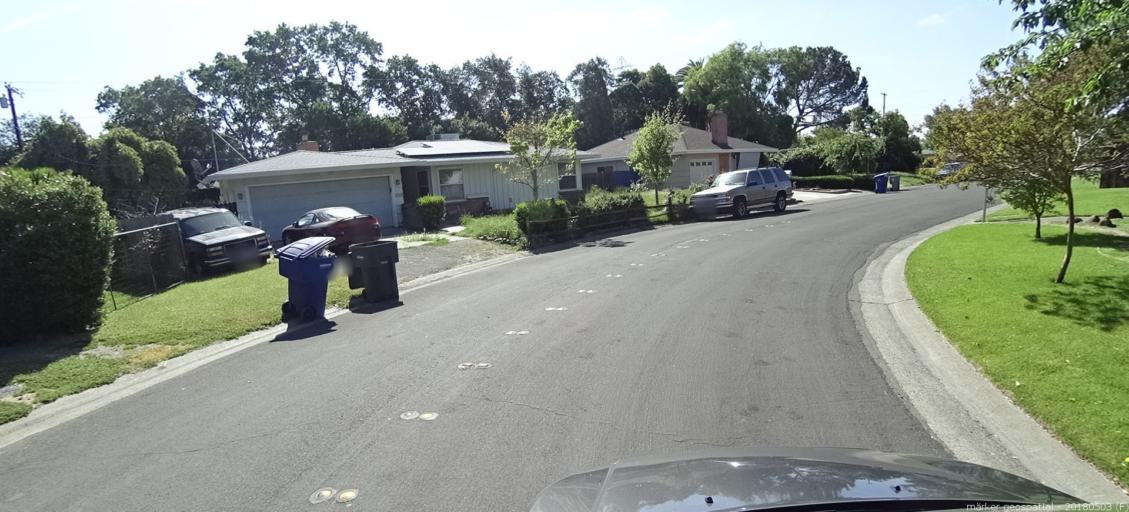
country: US
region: California
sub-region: Sacramento County
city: Arden-Arcade
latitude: 38.6276
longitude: -121.4224
